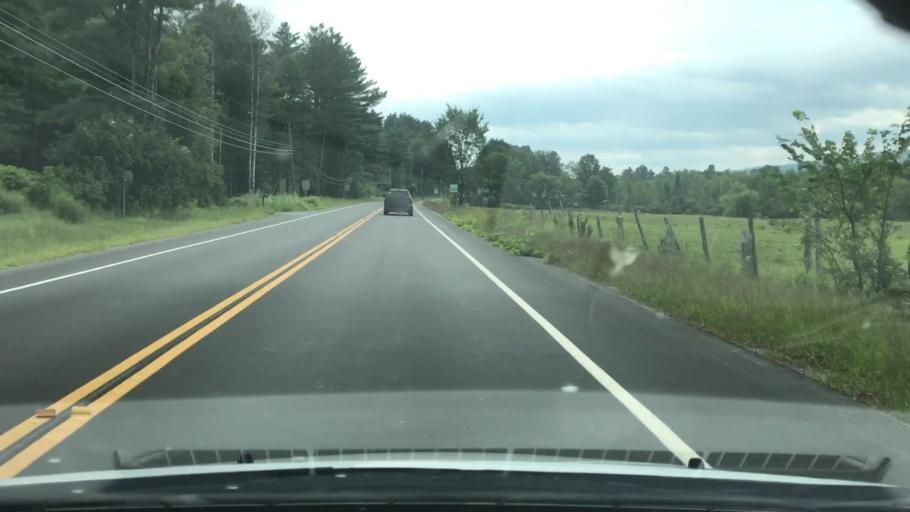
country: US
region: New Hampshire
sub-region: Grafton County
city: Orford
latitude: 43.8939
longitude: -72.1482
